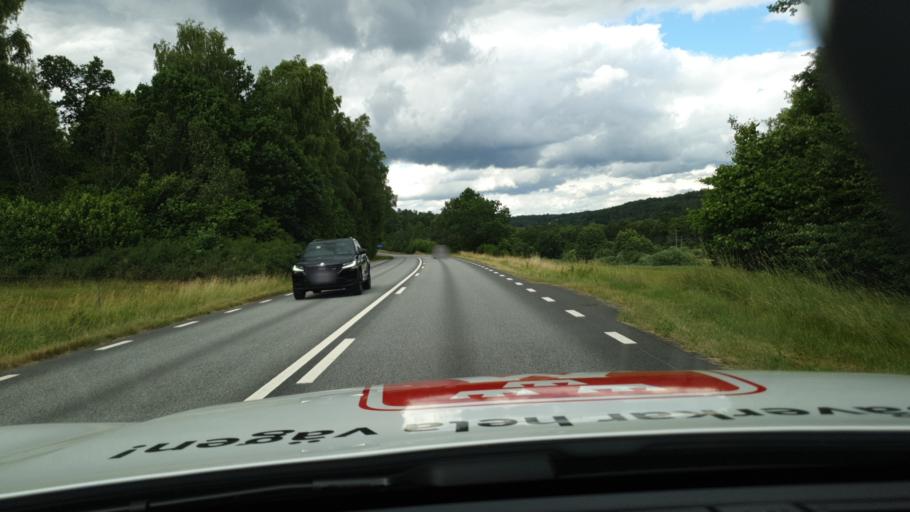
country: SE
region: Skane
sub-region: Hassleholms Kommun
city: Tormestorp
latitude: 56.0959
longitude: 13.7379
